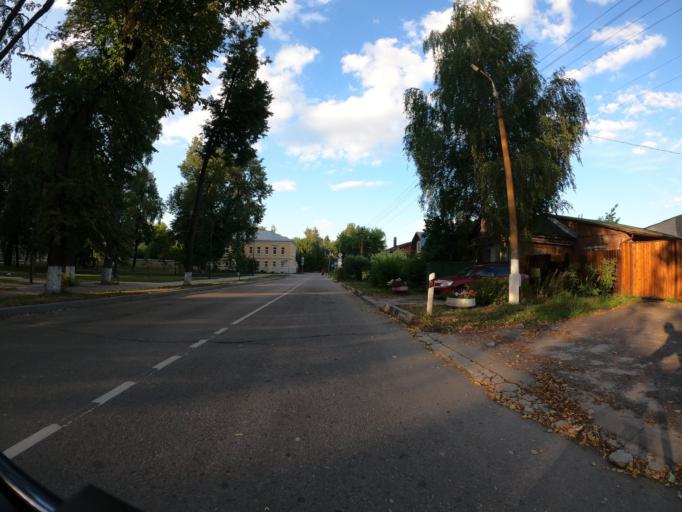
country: RU
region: Moskovskaya
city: Raduzhnyy
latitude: 55.1091
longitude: 38.7435
